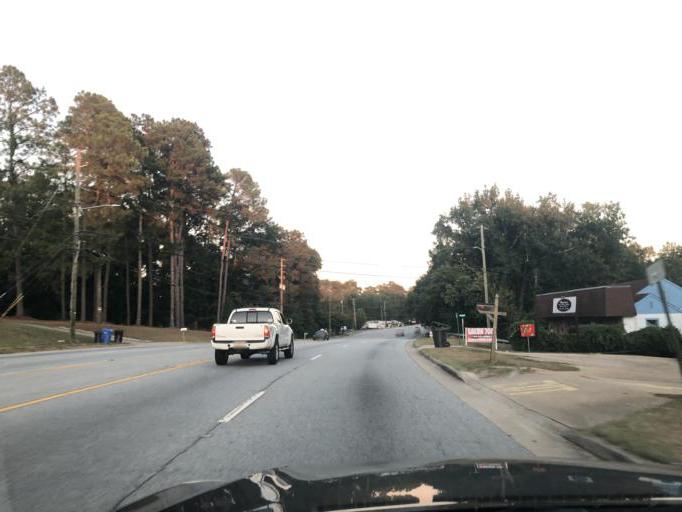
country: US
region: Georgia
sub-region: Muscogee County
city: Columbus
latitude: 32.4676
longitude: -84.9052
